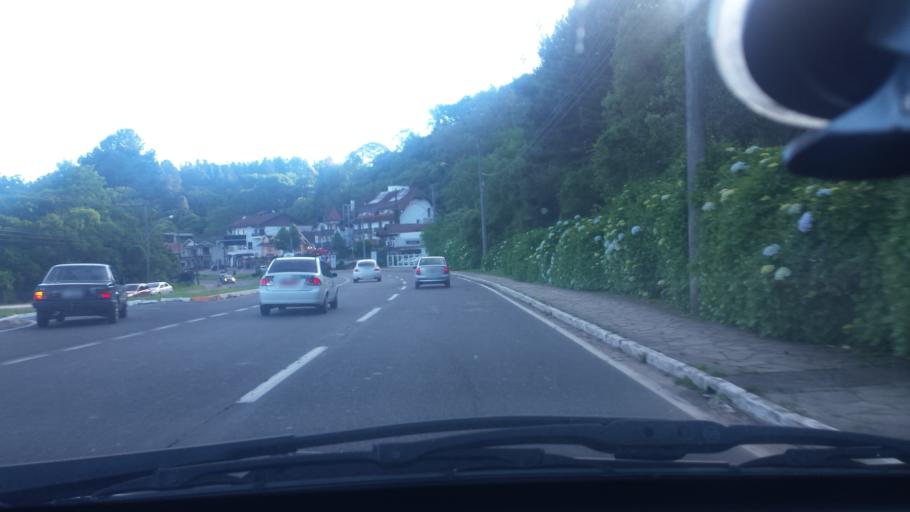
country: BR
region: Rio Grande do Sul
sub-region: Canela
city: Canela
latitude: -29.3723
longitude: -50.8641
